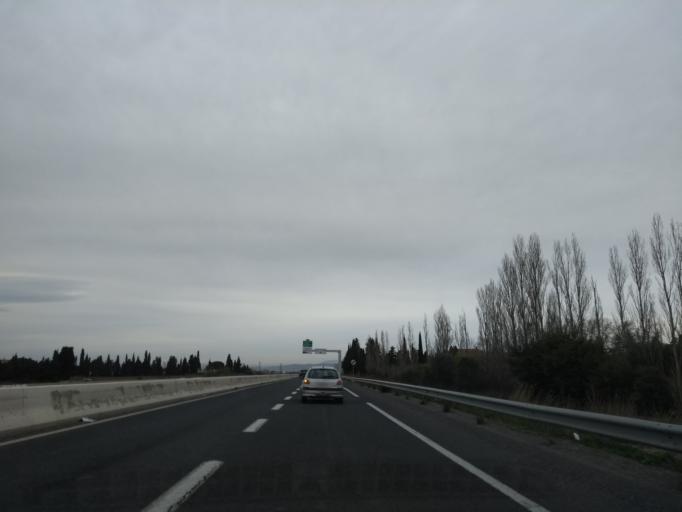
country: FR
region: Languedoc-Roussillon
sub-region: Departement des Pyrenees-Orientales
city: Toulouges
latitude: 42.6722
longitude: 2.8571
